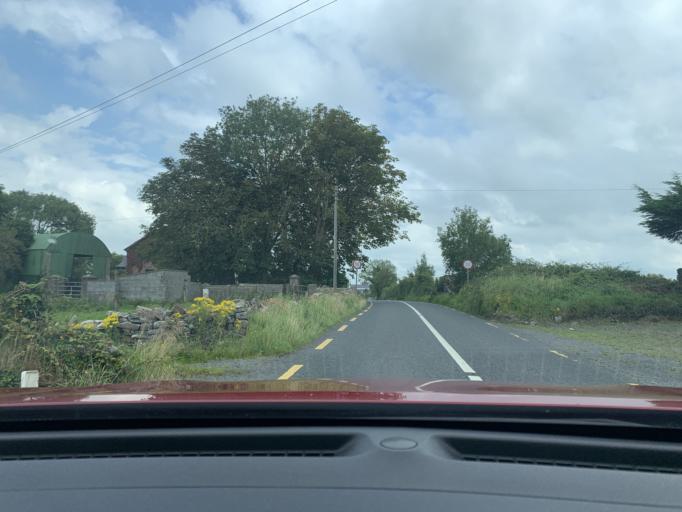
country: IE
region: Connaught
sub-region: Maigh Eo
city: Kiltamagh
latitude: 53.8427
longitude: -9.0114
